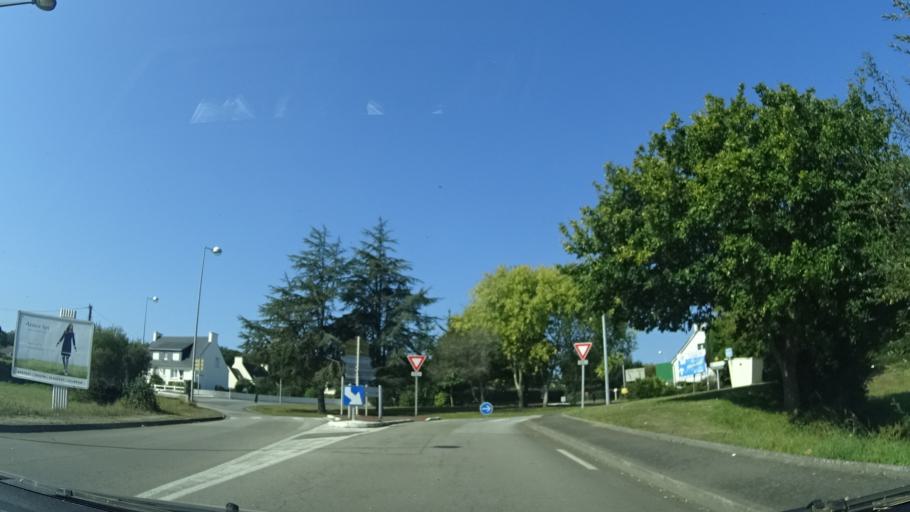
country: FR
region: Brittany
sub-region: Departement du Finistere
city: Douarnenez
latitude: 48.0860
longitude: -4.3456
